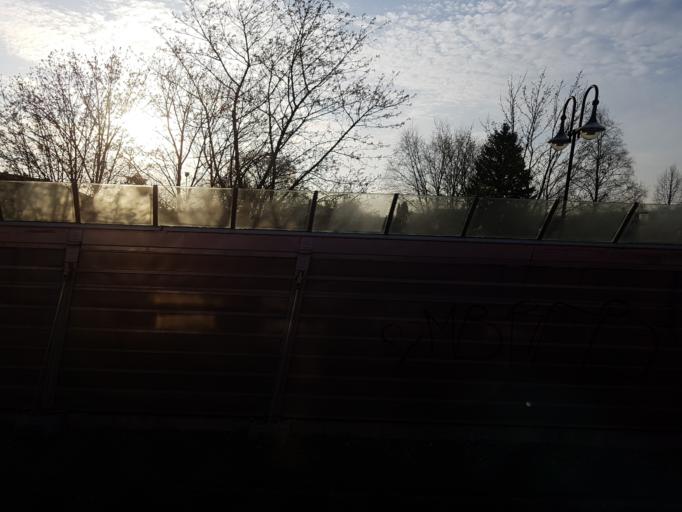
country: NO
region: Akershus
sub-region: Ullensaker
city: Klofta
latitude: 60.0739
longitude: 11.1395
